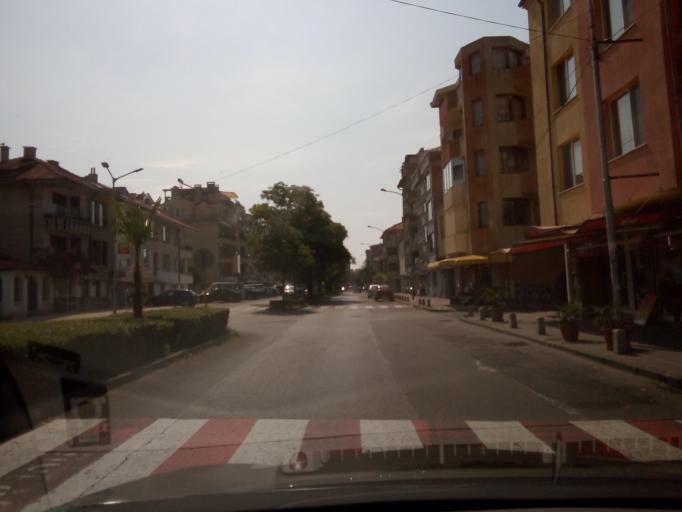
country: BG
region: Burgas
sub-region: Obshtina Pomorie
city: Pomorie
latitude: 42.5608
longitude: 27.6351
